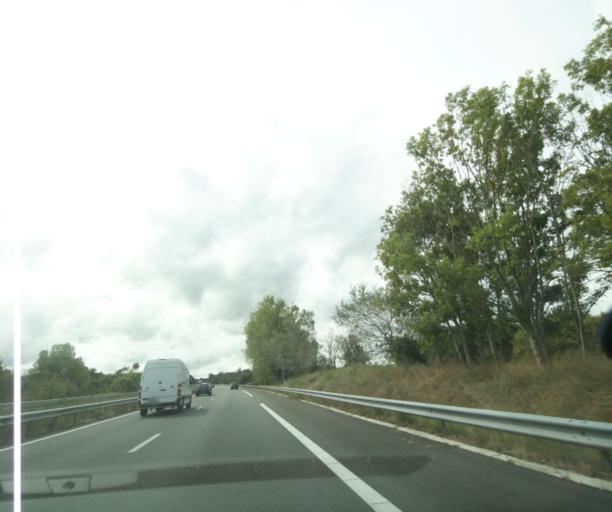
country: FR
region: Poitou-Charentes
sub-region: Departement de la Charente-Maritime
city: Saint-Genis-de-Saintonge
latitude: 45.4744
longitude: -0.6205
